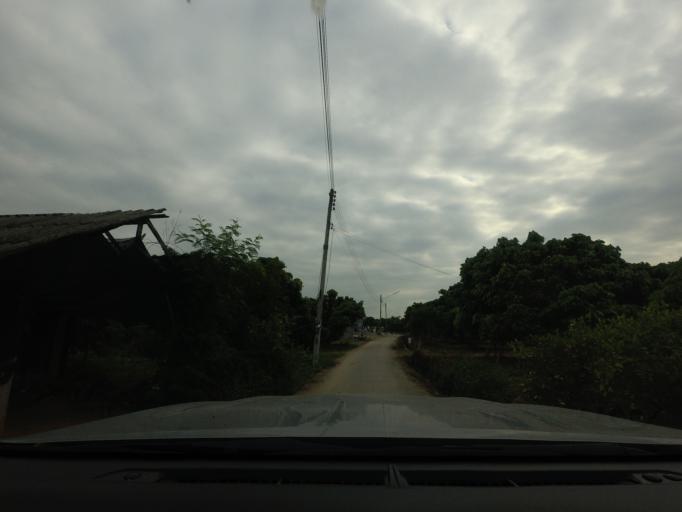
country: TH
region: Chiang Mai
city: Saraphi
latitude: 18.7018
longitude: 98.9980
